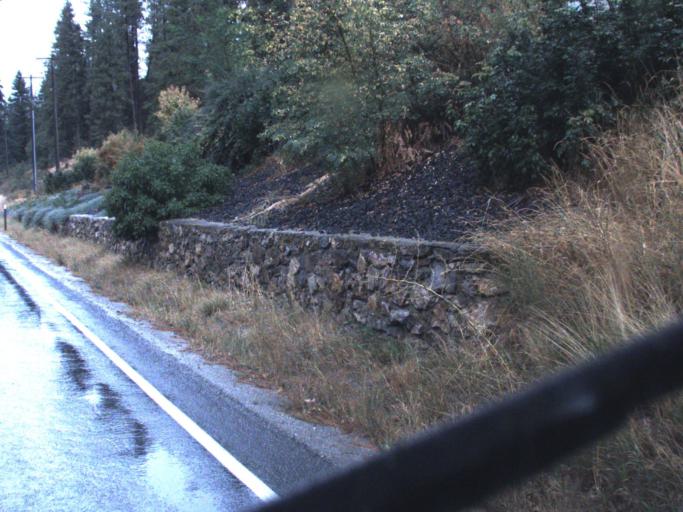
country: US
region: Washington
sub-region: Stevens County
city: Chewelah
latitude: 48.1698
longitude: -117.7229
